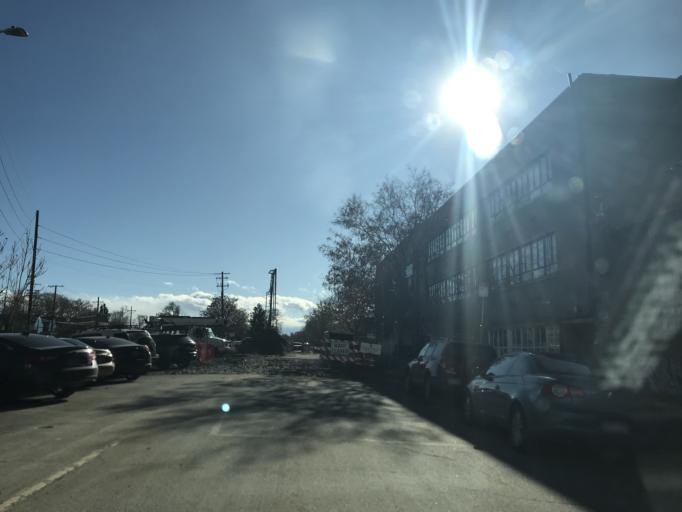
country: US
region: Colorado
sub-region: Denver County
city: Denver
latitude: 39.7720
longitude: -104.9661
